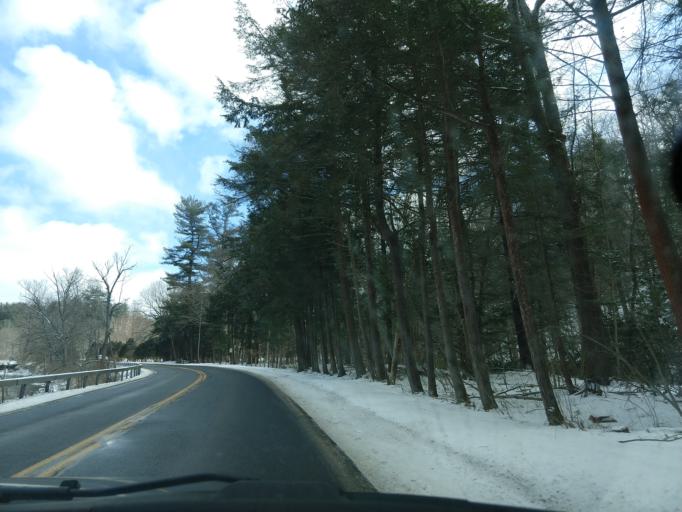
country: US
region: New York
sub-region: Tompkins County
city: Northeast Ithaca
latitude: 42.4530
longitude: -76.4602
